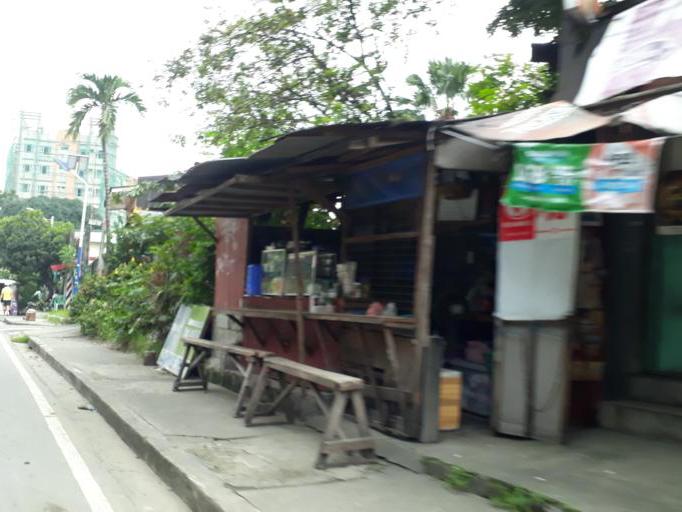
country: PH
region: Calabarzon
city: Bagong Pagasa
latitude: 14.6627
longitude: 121.0432
